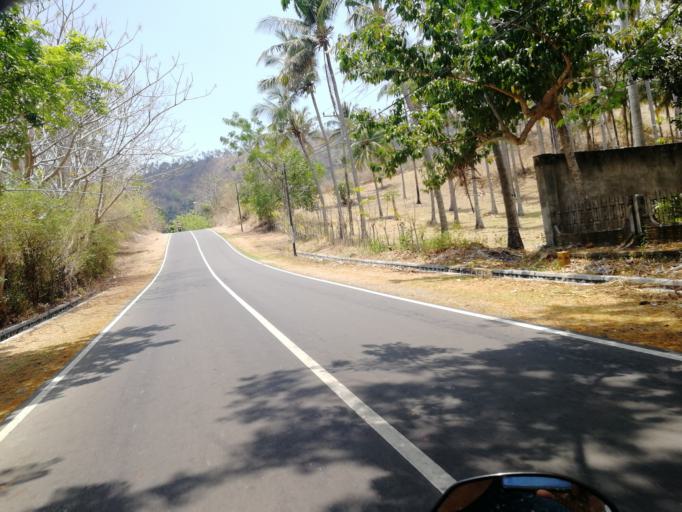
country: ID
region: West Nusa Tenggara
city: Karangsubagan
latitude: -8.4563
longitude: 116.0392
